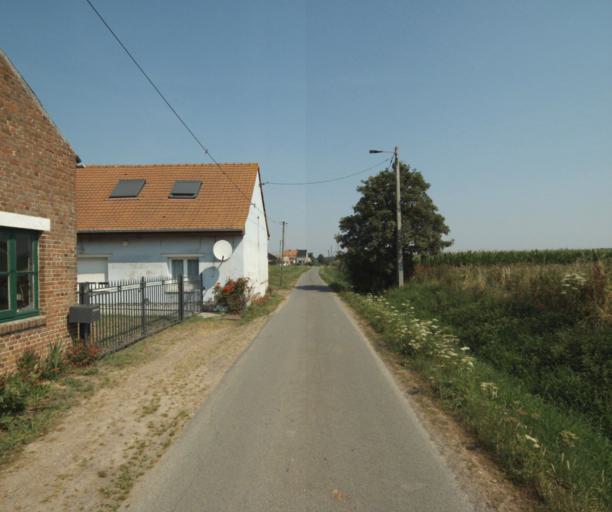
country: FR
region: Nord-Pas-de-Calais
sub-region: Departement du Nord
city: Quesnoy-sur-Deule
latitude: 50.7084
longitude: 2.9740
